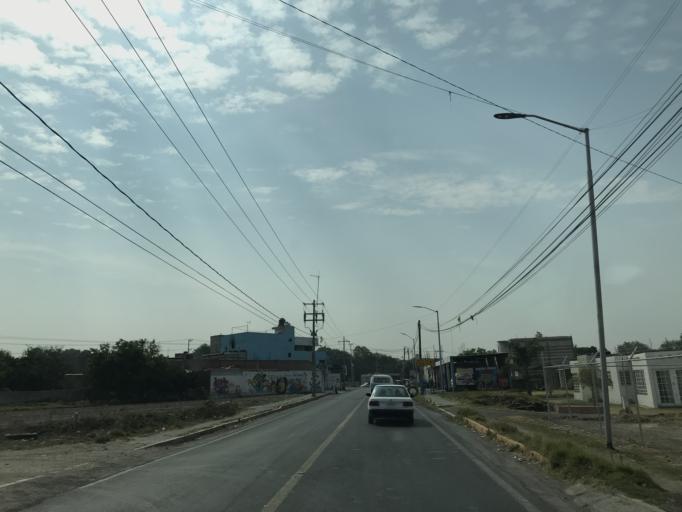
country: MX
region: Tlaxcala
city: Tenancingo
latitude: 19.1426
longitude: -98.1924
